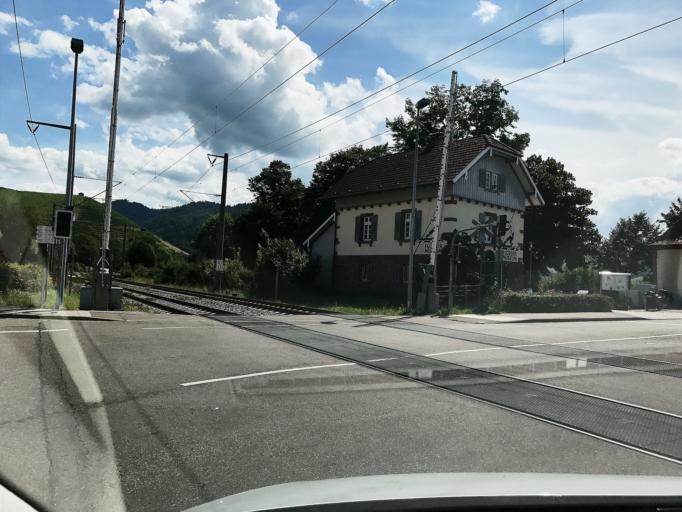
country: DE
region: Hesse
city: Gengenbach
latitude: 48.4028
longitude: 8.0159
